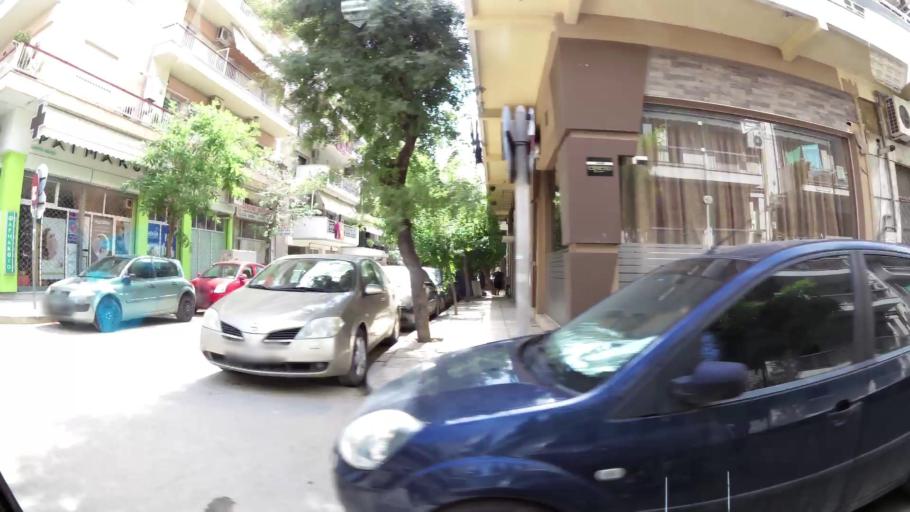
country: GR
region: Central Macedonia
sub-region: Nomos Thessalonikis
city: Triandria
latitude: 40.6064
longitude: 22.9614
